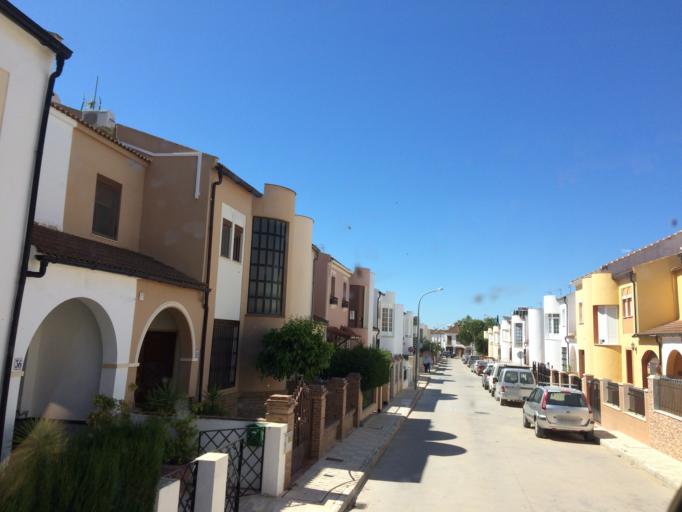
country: ES
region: Andalusia
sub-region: Provincia de Malaga
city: Campillos
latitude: 37.0474
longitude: -4.8676
